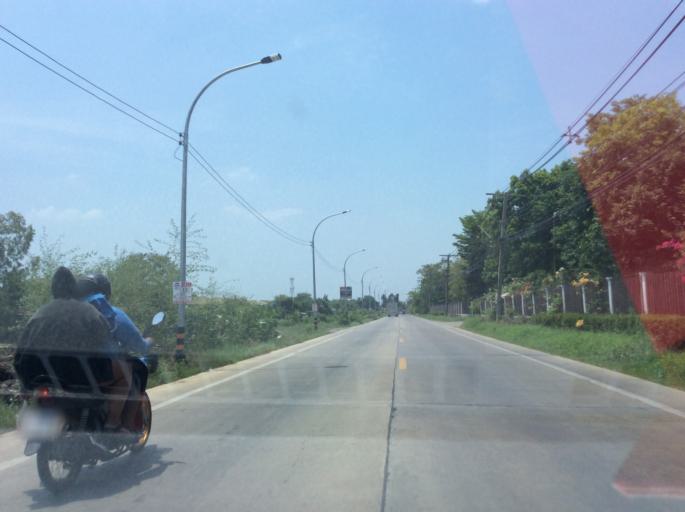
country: TH
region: Pathum Thani
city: Ban Rangsit
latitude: 14.0308
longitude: 100.7788
